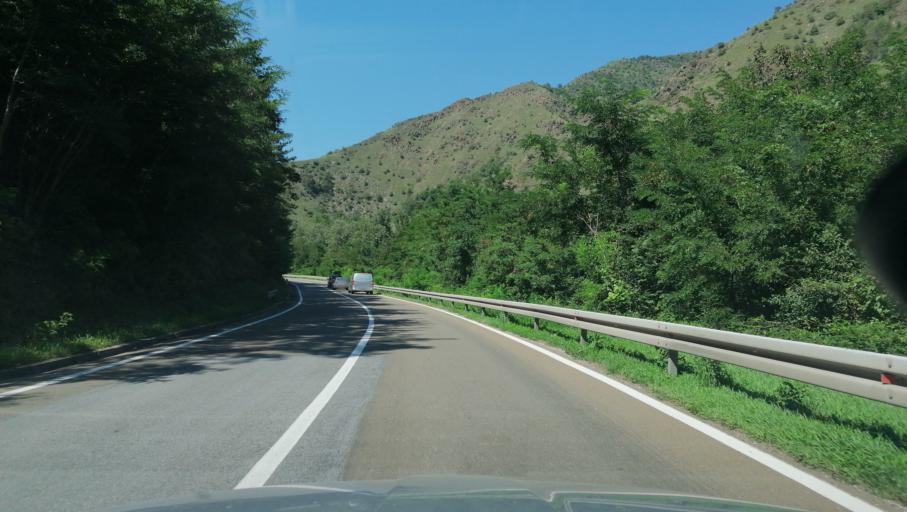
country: RS
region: Central Serbia
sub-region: Raski Okrug
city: Kraljevo
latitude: 43.5794
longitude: 20.5864
